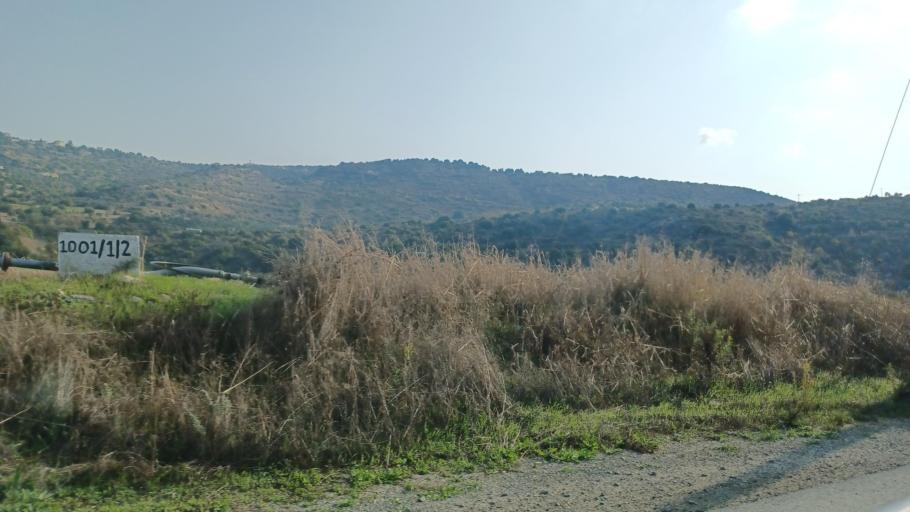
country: CY
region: Pafos
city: Polis
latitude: 34.9811
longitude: 32.4732
